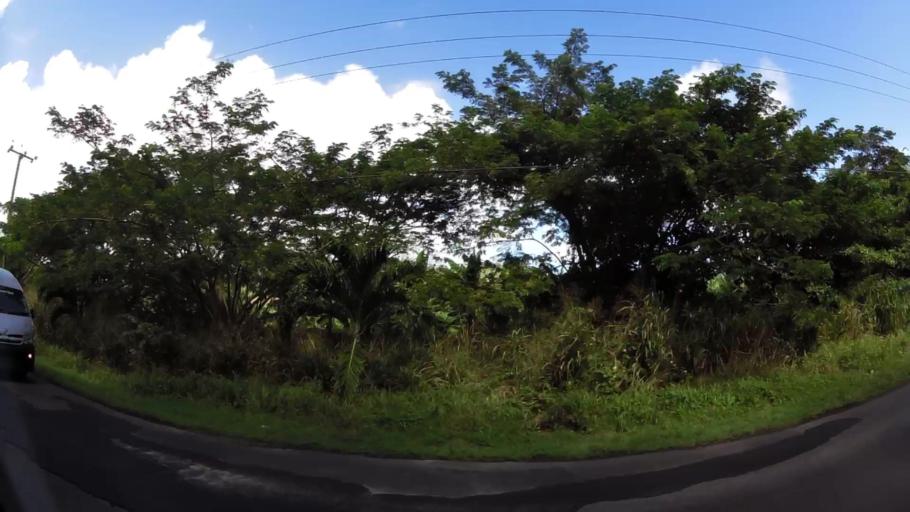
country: LC
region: Dennery Quarter
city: Dennery
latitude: 13.9273
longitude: -60.8988
